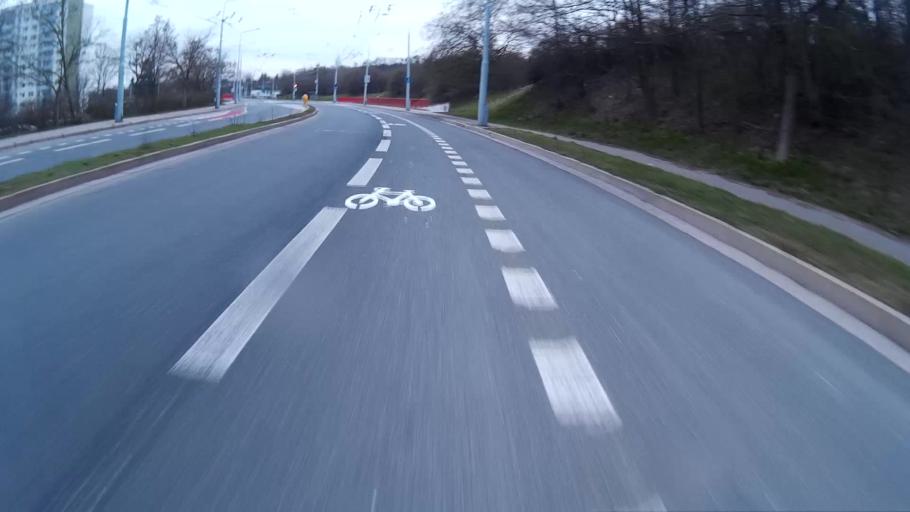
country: CZ
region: South Moravian
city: Ostopovice
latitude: 49.1801
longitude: 16.5497
